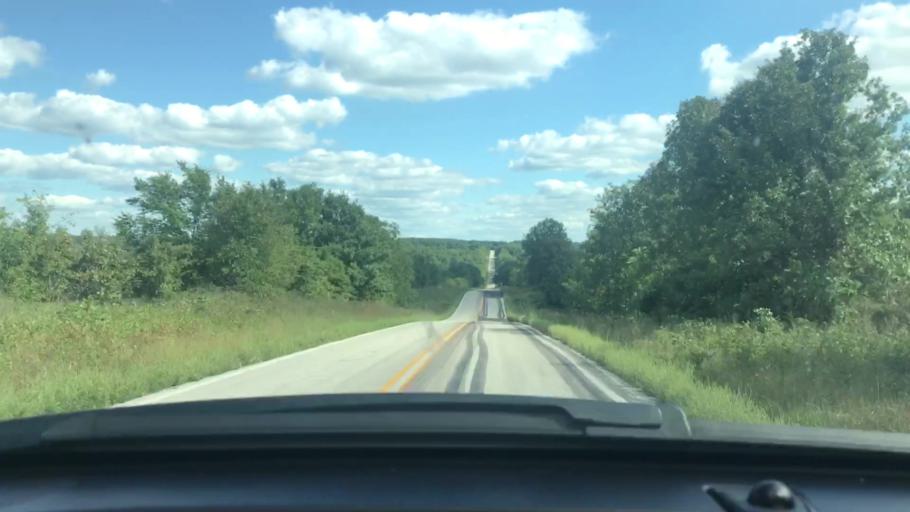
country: US
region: Missouri
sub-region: Wright County
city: Hartville
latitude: 37.3888
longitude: -92.4464
